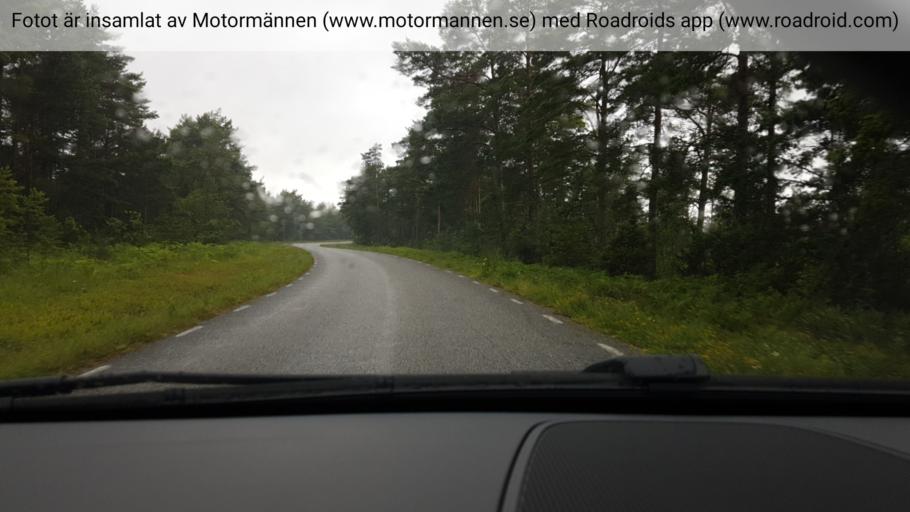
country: SE
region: Gotland
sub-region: Gotland
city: Slite
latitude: 57.8610
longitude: 18.8507
